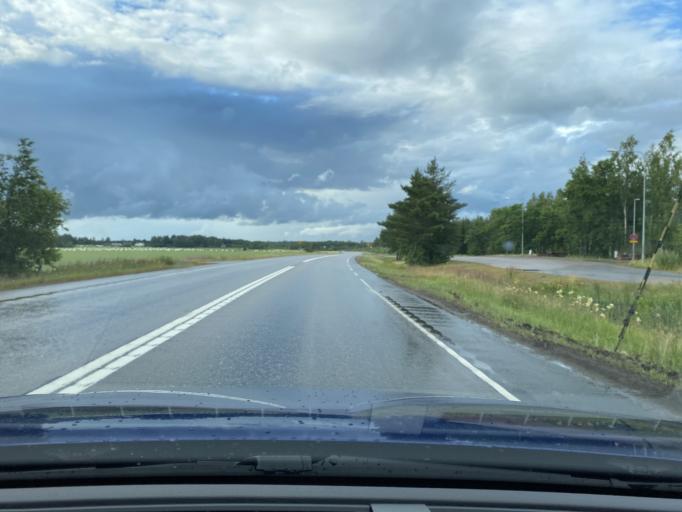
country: FI
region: Uusimaa
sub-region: Helsinki
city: Nurmijaervi
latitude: 60.5186
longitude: 24.8430
